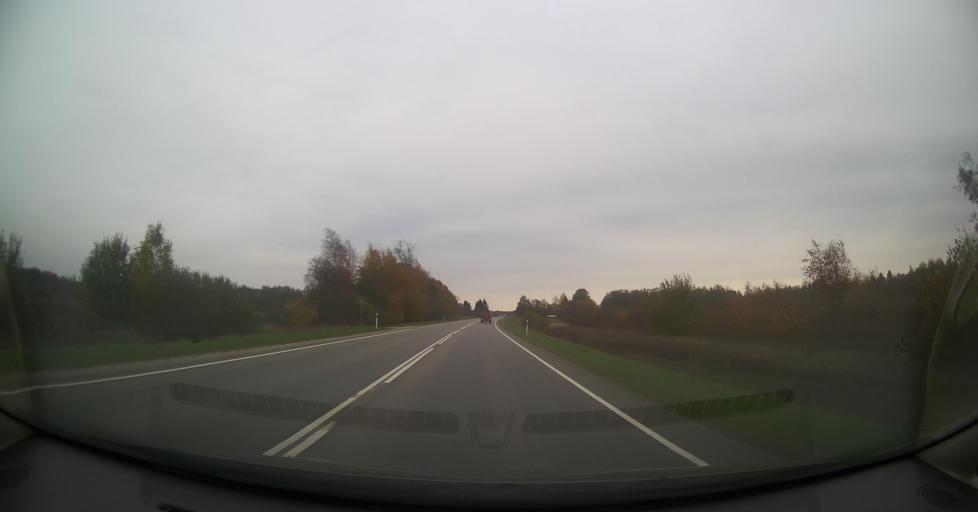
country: EE
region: Laeaene
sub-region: Ridala Parish
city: Uuemoisa
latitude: 58.9736
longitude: 23.8533
